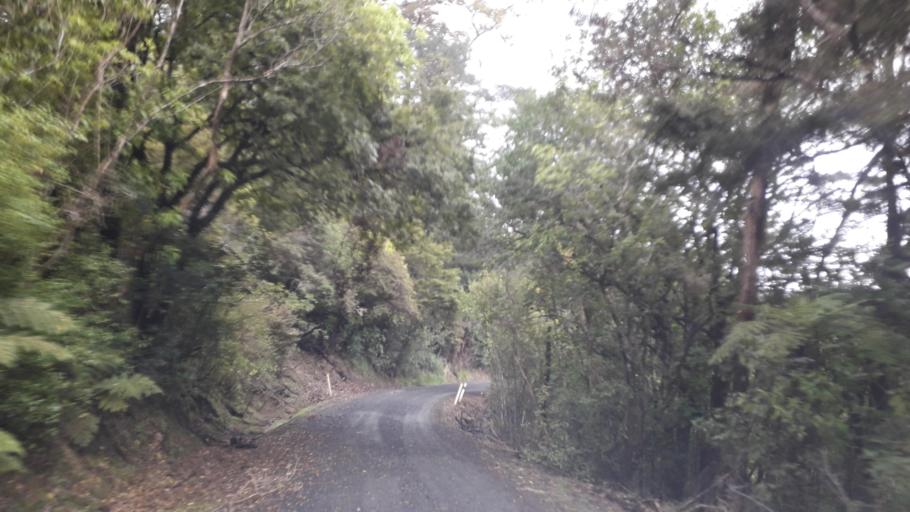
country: NZ
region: Northland
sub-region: Far North District
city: Waimate North
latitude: -35.3152
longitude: 173.5680
